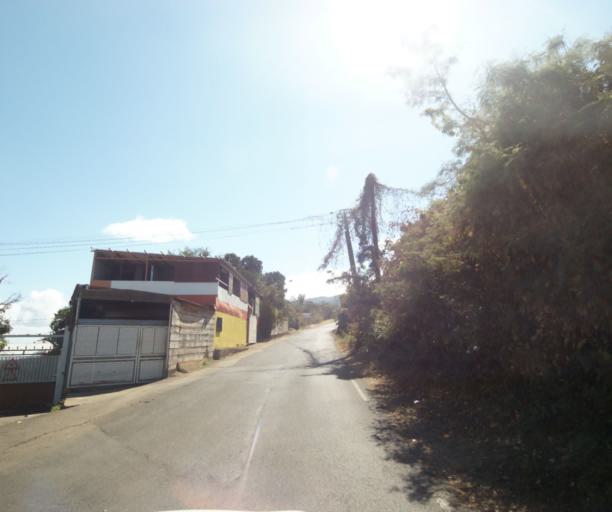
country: RE
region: Reunion
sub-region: Reunion
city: Saint-Paul
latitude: -20.9891
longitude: 55.3252
